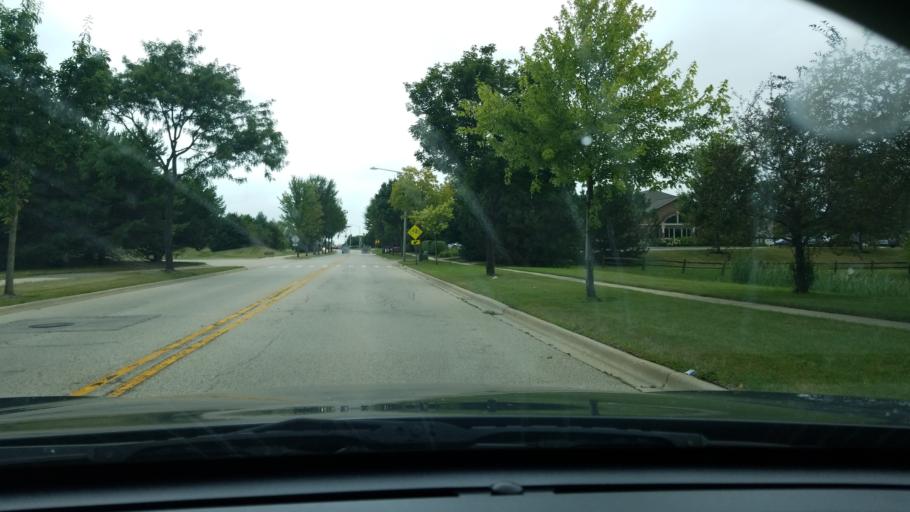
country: US
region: Illinois
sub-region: McHenry County
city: Lake in the Hills
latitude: 42.1685
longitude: -88.3313
